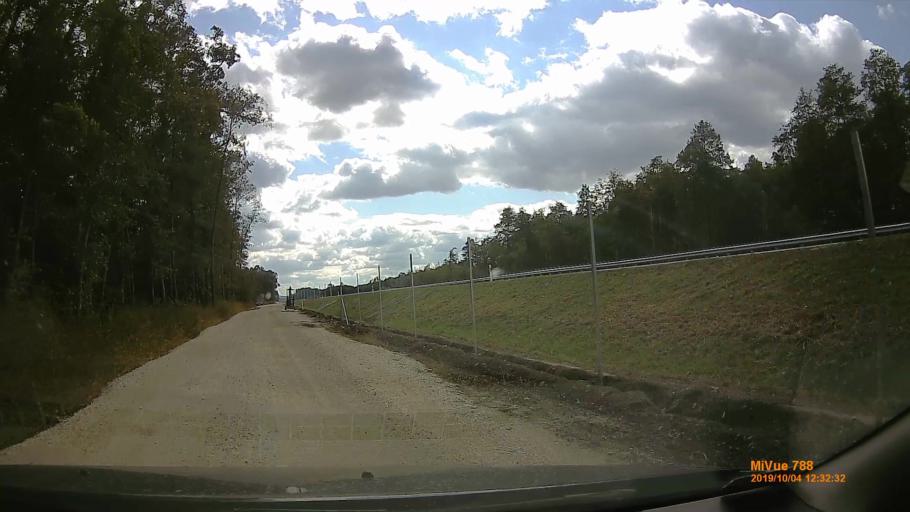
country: HU
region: Somogy
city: Karad
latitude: 46.6941
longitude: 17.7702
